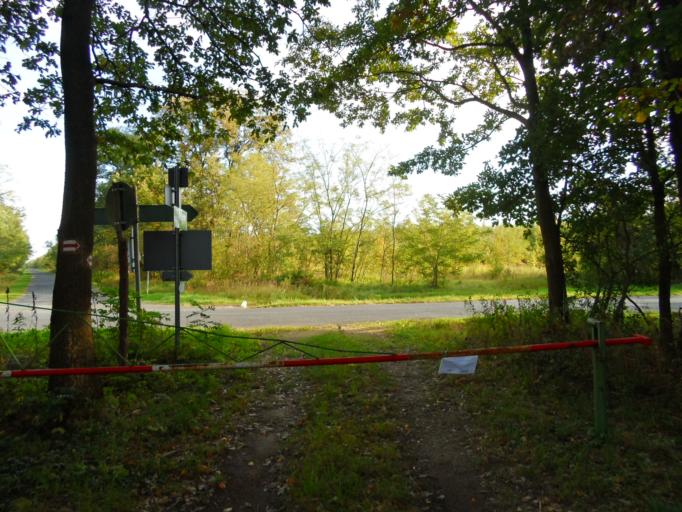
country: HU
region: Veszprem
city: Devecser
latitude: 47.2020
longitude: 17.4190
